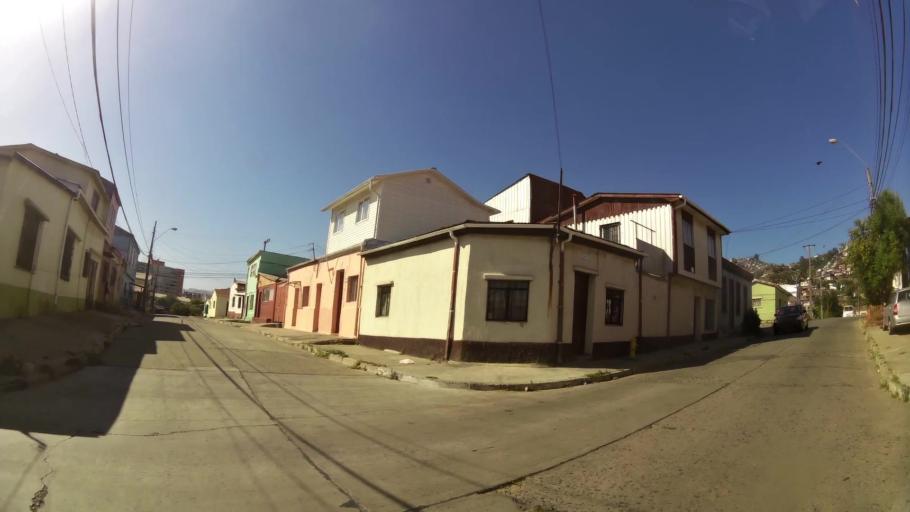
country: CL
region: Valparaiso
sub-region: Provincia de Valparaiso
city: Valparaiso
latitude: -33.0435
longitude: -71.6354
